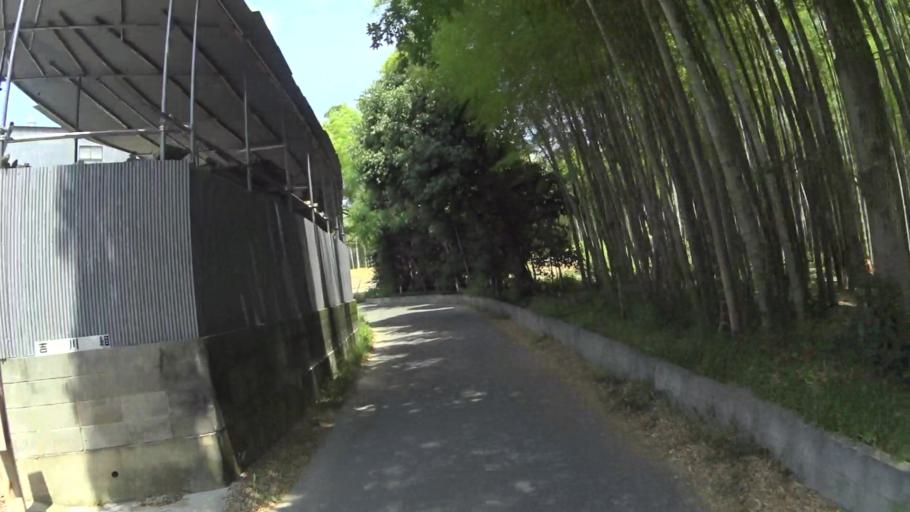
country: JP
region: Kyoto
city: Muko
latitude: 34.9435
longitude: 135.6814
